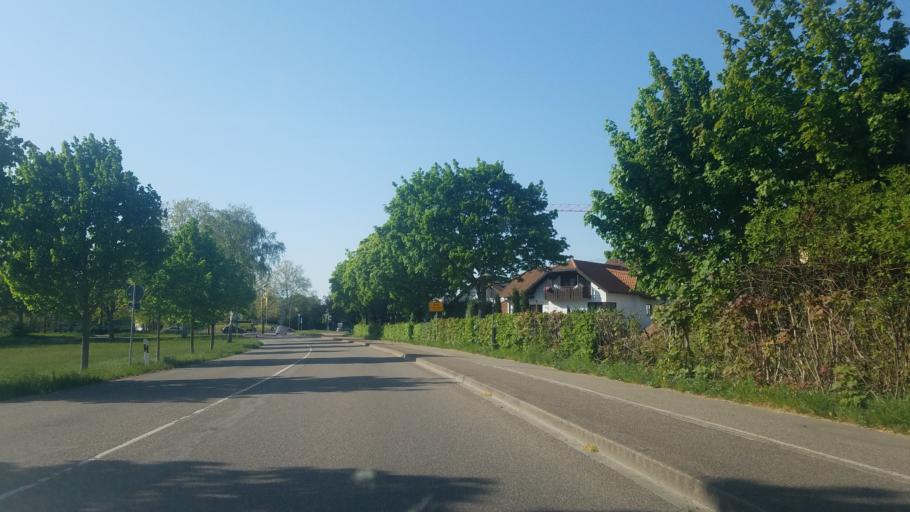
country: DE
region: Baden-Wuerttemberg
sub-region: Karlsruhe Region
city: Buhl
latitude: 48.6892
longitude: 8.1338
